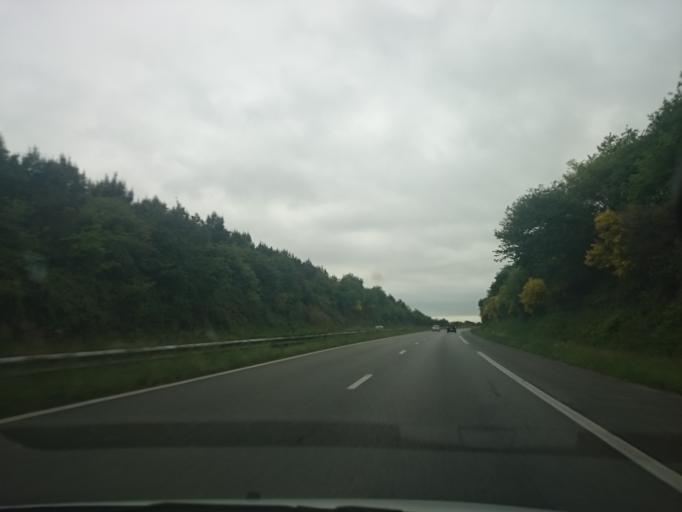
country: FR
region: Brittany
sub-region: Departement du Finistere
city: Le Trevoux
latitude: 47.8782
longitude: -3.6632
